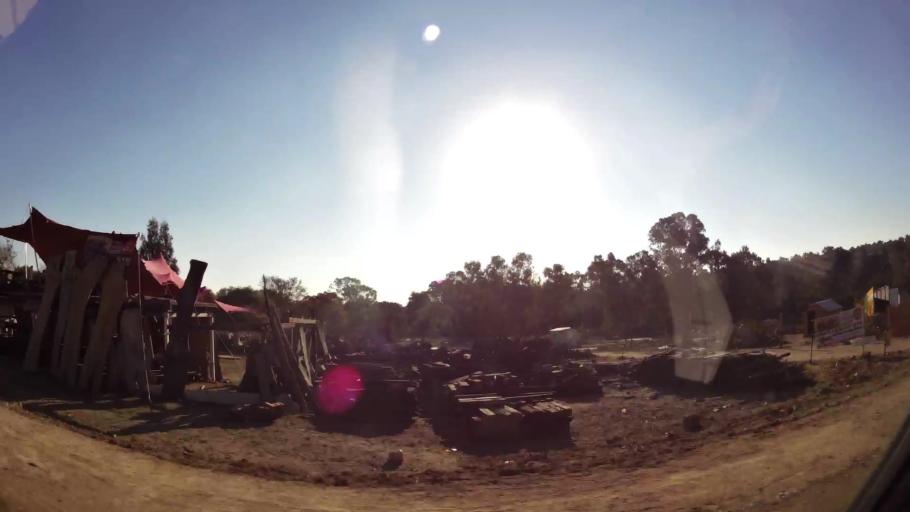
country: ZA
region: Gauteng
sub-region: City of Johannesburg Metropolitan Municipality
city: Midrand
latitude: -25.9795
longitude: 28.0768
